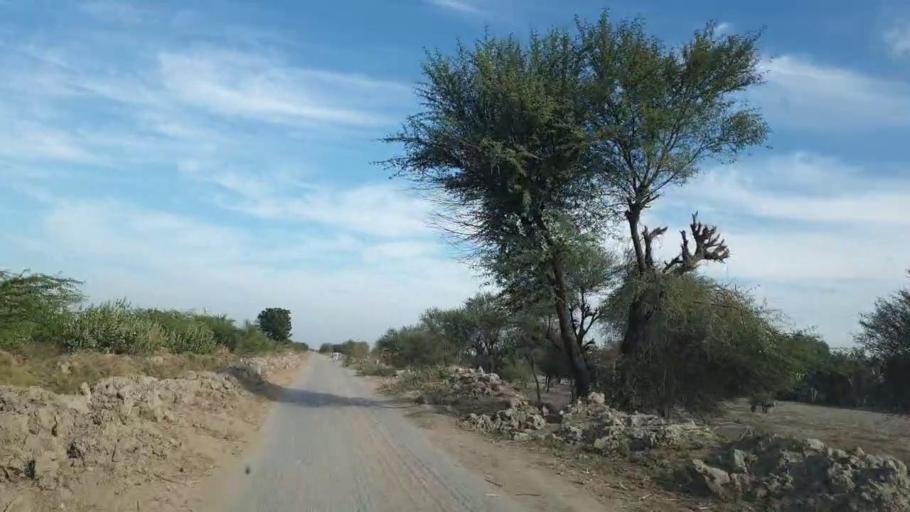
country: PK
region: Sindh
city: Pithoro
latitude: 25.6459
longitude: 69.3519
